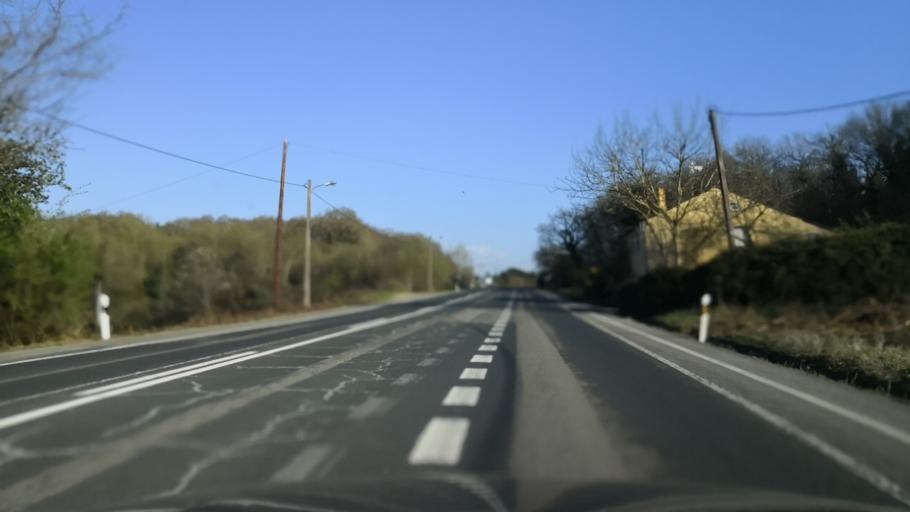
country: ES
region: Galicia
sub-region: Provincia de Lugo
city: Corgo
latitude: 42.9560
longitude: -7.4678
